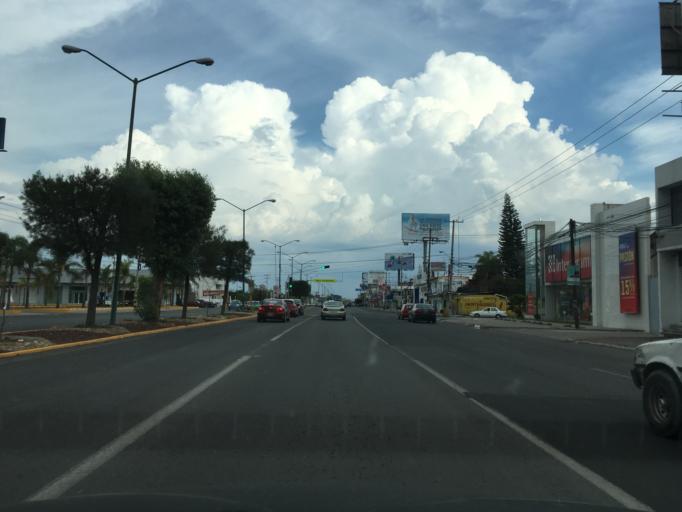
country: MX
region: Guanajuato
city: Celaya
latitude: 20.5480
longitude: -100.8219
